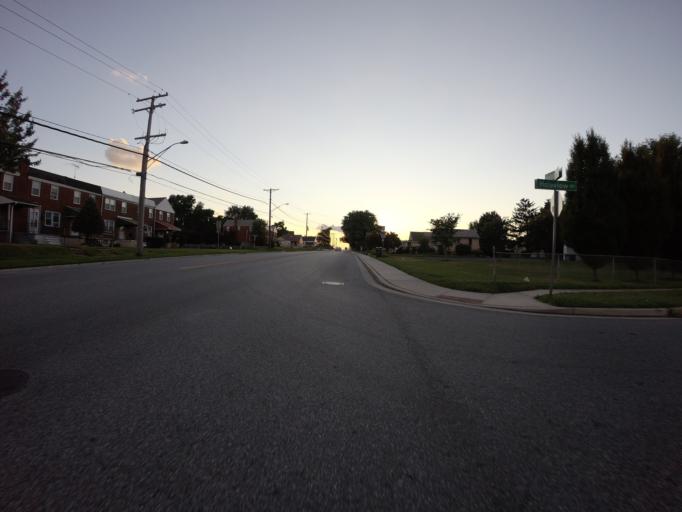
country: US
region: Maryland
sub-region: Baltimore County
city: Dundalk
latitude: 39.2715
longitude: -76.5086
